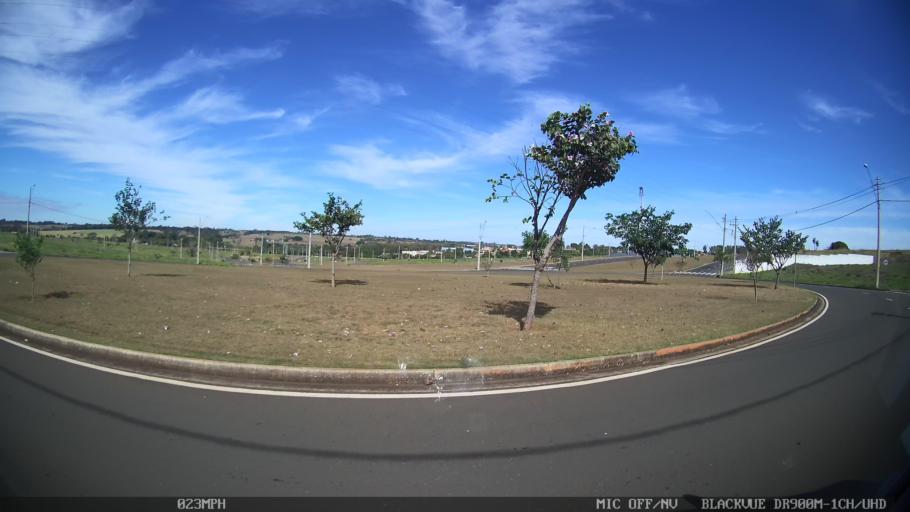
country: BR
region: Sao Paulo
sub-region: Sao Jose Do Rio Preto
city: Sao Jose do Rio Preto
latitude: -20.8547
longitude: -49.3788
